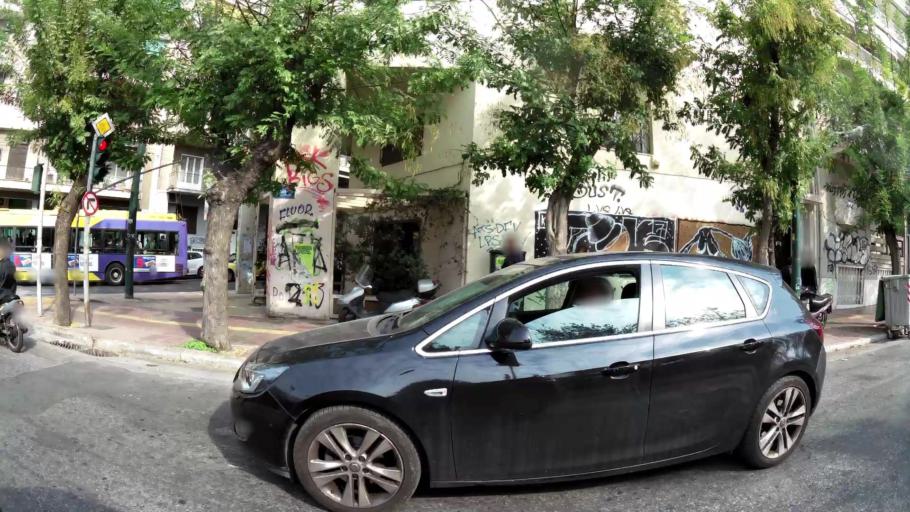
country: GR
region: Attica
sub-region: Nomarchia Athinas
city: Kipseli
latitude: 37.9953
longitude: 23.7342
